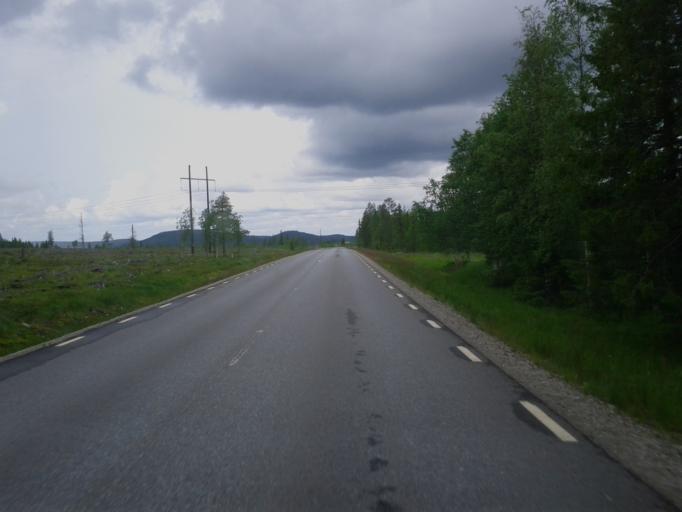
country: SE
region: Vaesterbotten
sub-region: Mala Kommun
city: Mala
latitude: 65.0680
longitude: 19.0342
